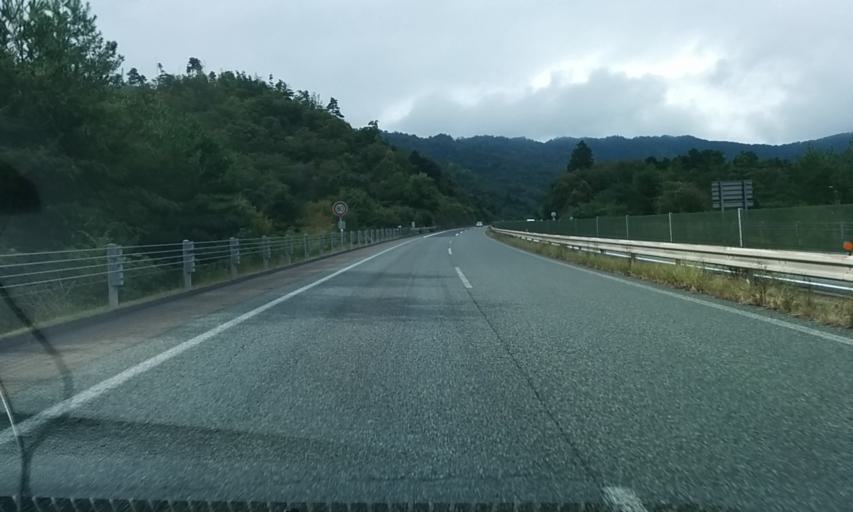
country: JP
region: Kyoto
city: Ayabe
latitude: 35.2298
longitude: 135.1887
